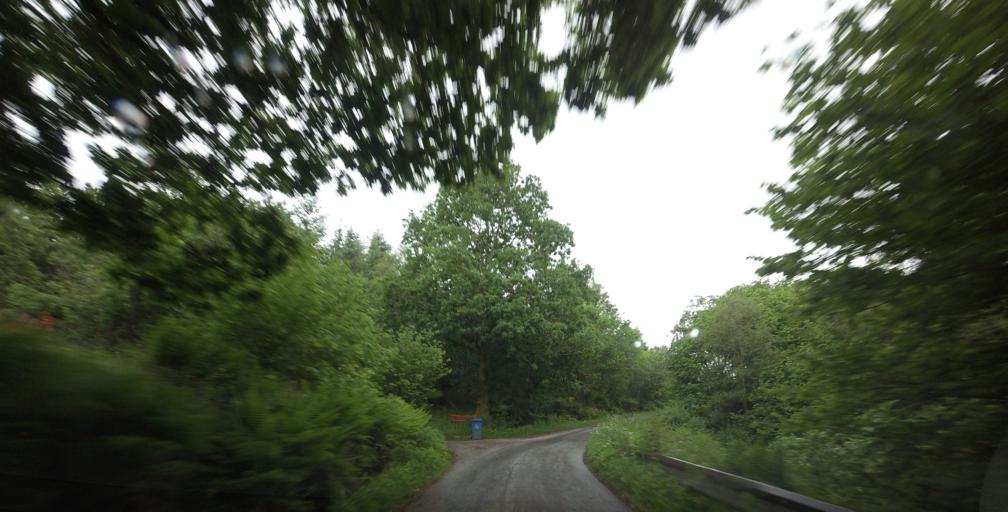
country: GB
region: Scotland
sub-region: Argyll and Bute
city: Oban
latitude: 56.7102
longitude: -5.5636
